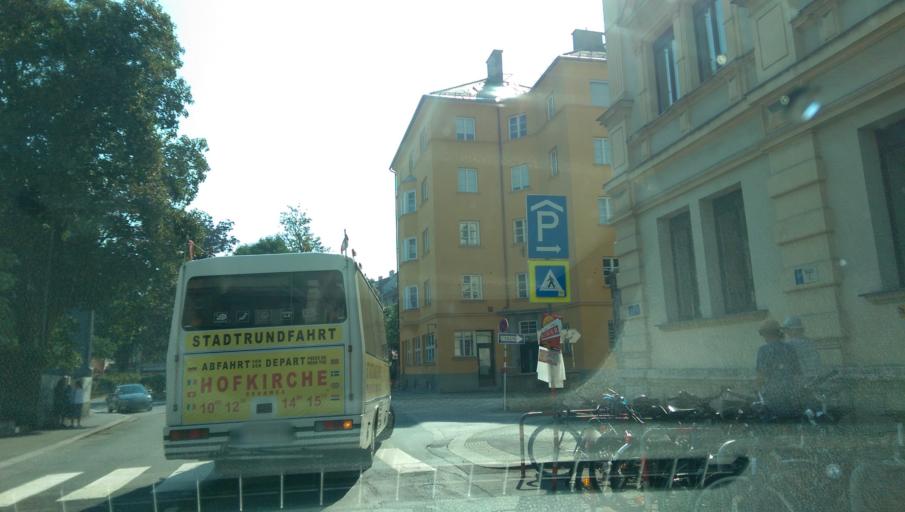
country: AT
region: Tyrol
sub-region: Innsbruck Stadt
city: Innsbruck
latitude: 47.2583
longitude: 11.3955
